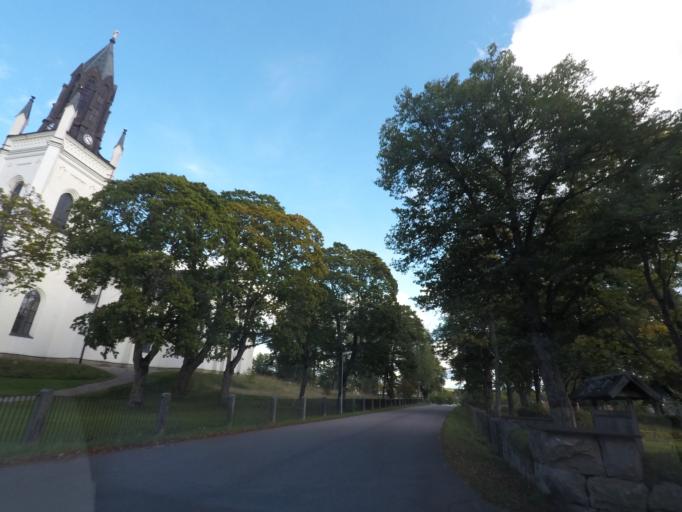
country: SE
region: Vaestmanland
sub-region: Skinnskattebergs Kommun
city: Skinnskatteberg
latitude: 59.8292
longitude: 15.6831
